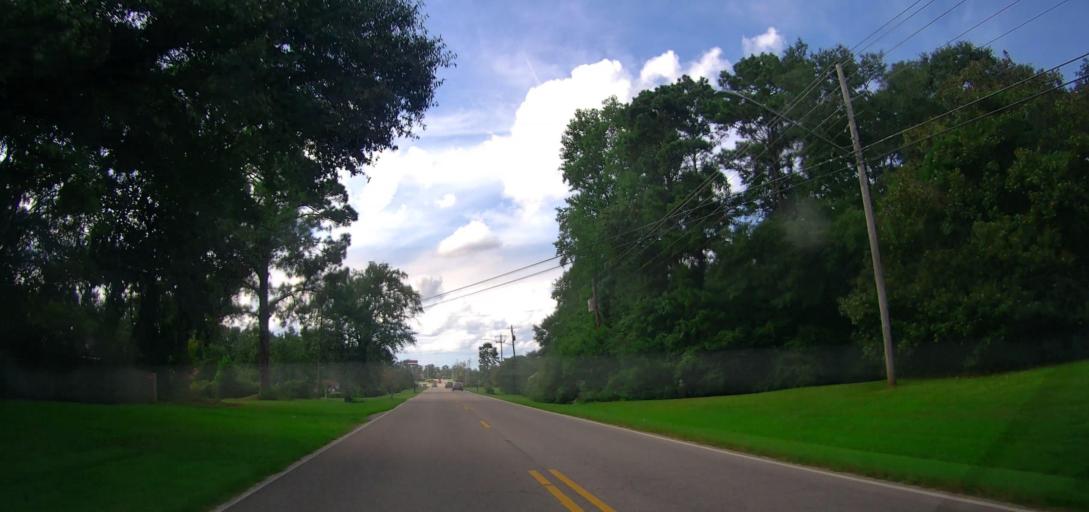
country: US
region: Alabama
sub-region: Russell County
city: Phenix City
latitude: 32.5172
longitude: -85.0261
